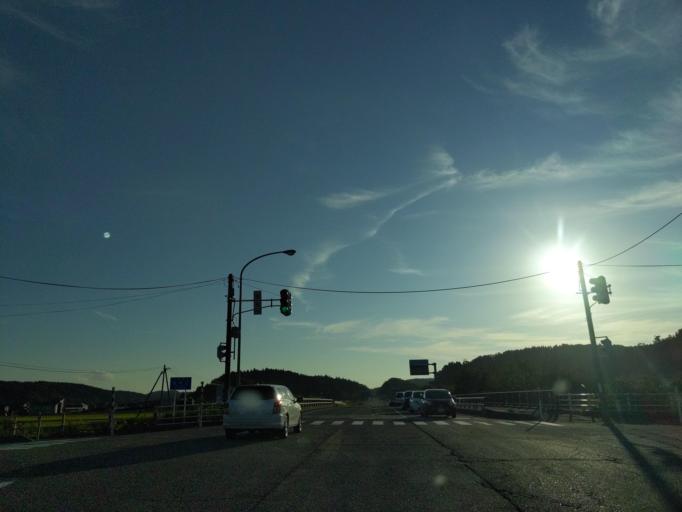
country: JP
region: Niigata
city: Nagaoka
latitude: 37.5712
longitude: 138.7433
